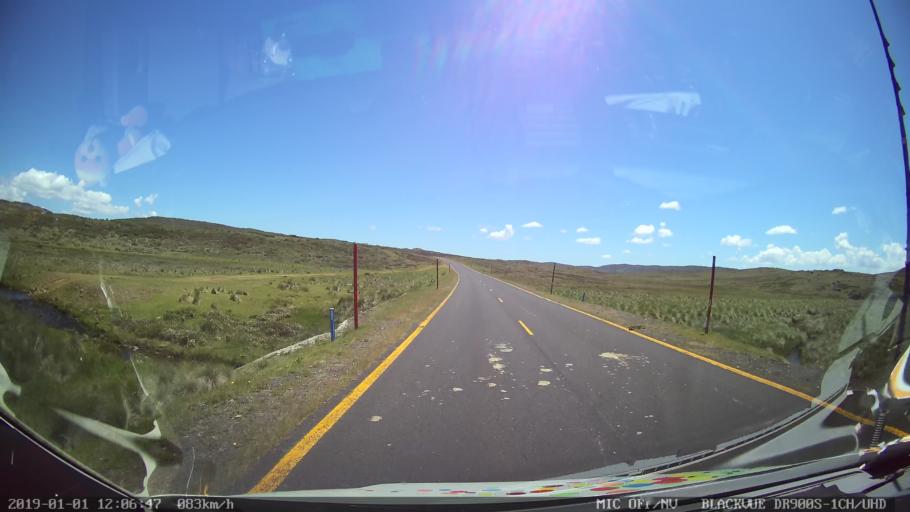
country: AU
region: New South Wales
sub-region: Snowy River
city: Jindabyne
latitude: -35.8410
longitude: 148.4912
